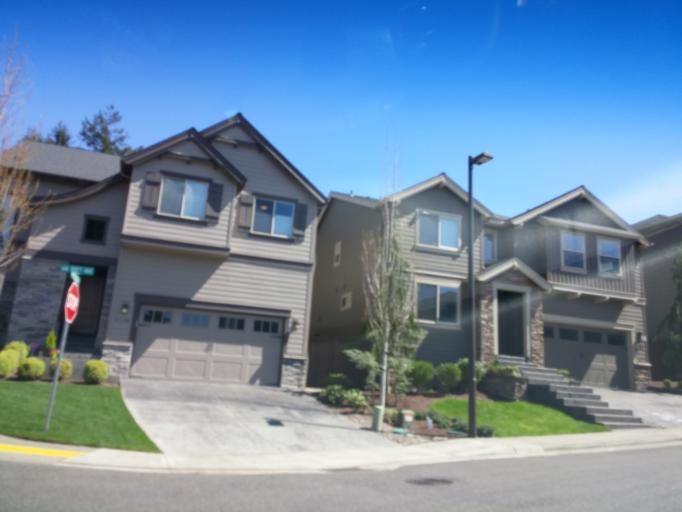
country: US
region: Oregon
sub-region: Washington County
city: West Haven
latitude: 45.5285
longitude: -122.7790
